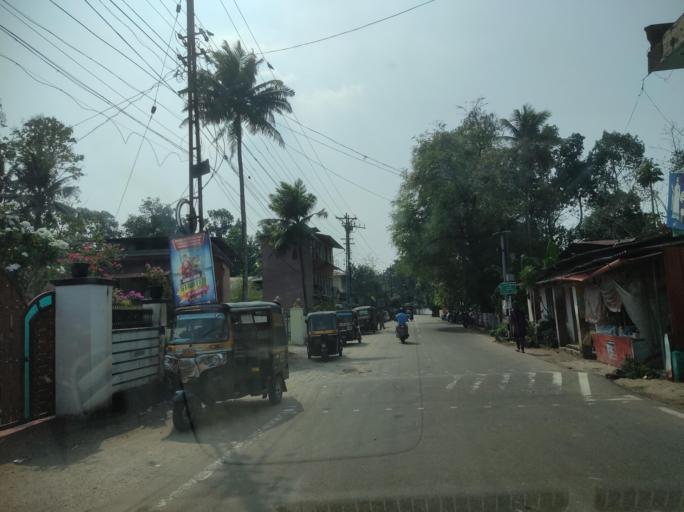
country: IN
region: Kerala
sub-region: Pattanamtitta
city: Tiruvalla
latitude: 9.3492
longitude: 76.5945
